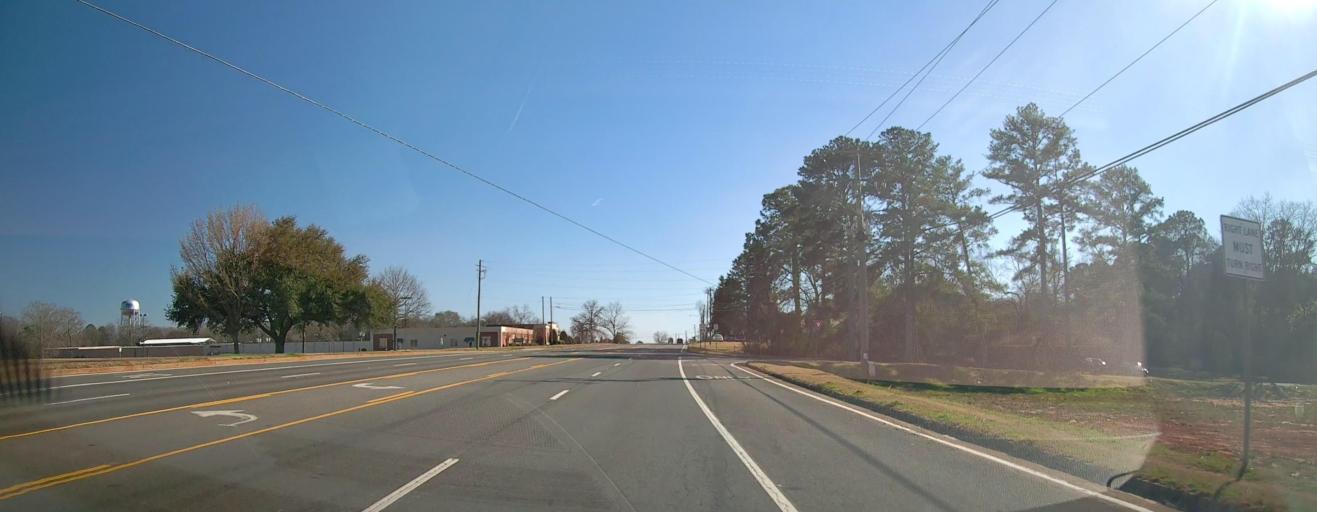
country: US
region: Georgia
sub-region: Sumter County
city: Americus
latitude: 32.0901
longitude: -84.2406
